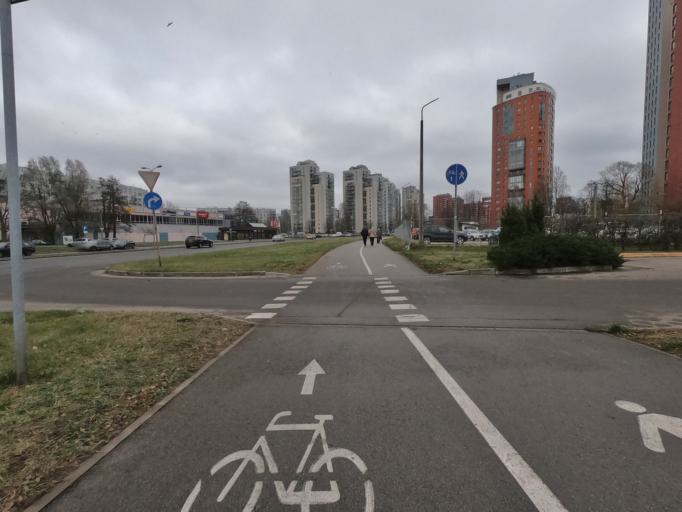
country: LV
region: Marupe
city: Marupe
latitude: 56.9592
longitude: 24.0115
